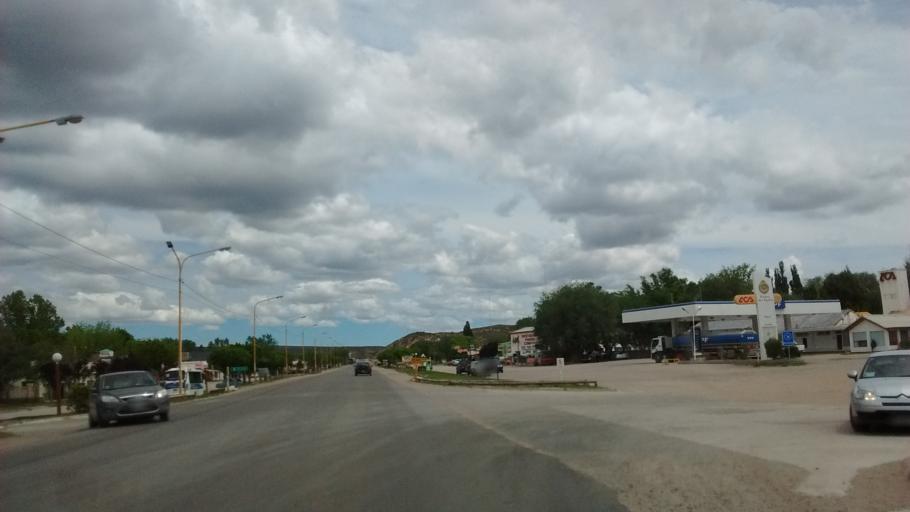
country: AR
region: Neuquen
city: Piedra del Aguila
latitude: -40.0482
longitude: -70.0762
